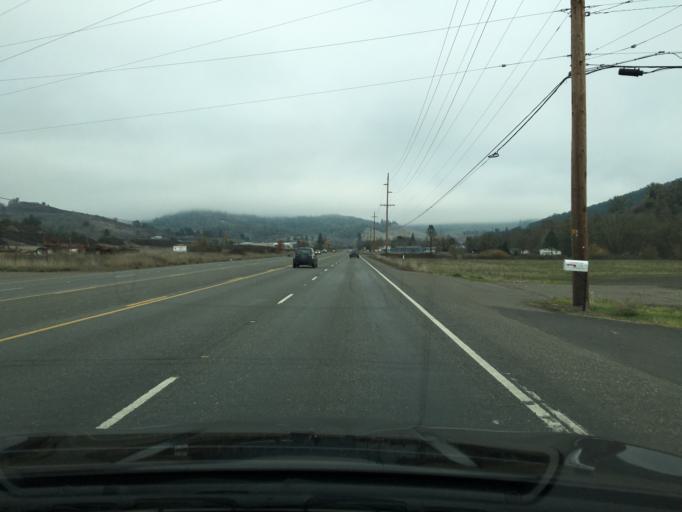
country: US
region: Oregon
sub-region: Douglas County
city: Roseburg
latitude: 43.2144
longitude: -123.2987
